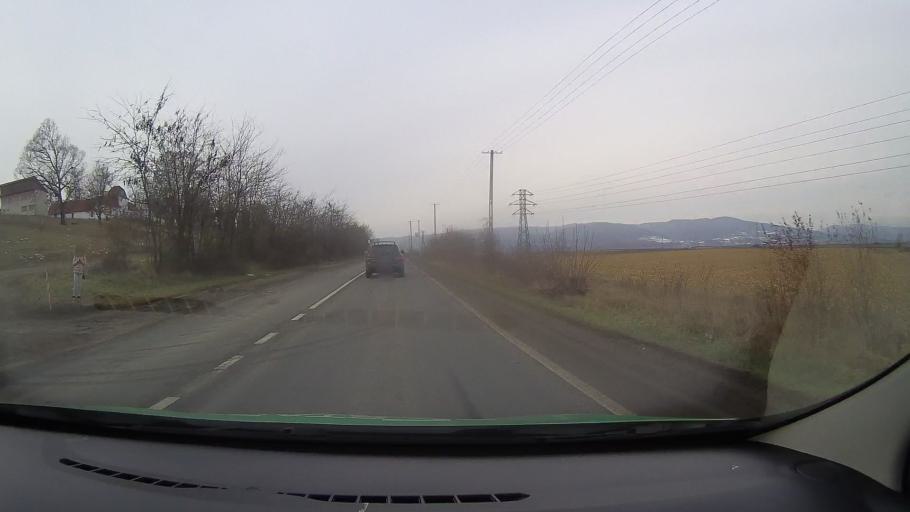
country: RO
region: Hunedoara
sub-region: Comuna Turdas
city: Pricaz
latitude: 45.8401
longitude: 23.1706
